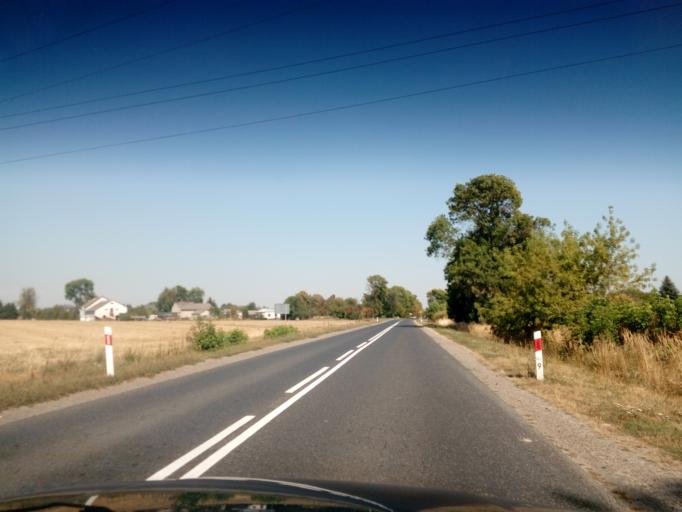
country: PL
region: Lublin Voivodeship
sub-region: Powiat hrubieszowski
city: Hrubieszow
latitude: 50.8159
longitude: 23.9288
